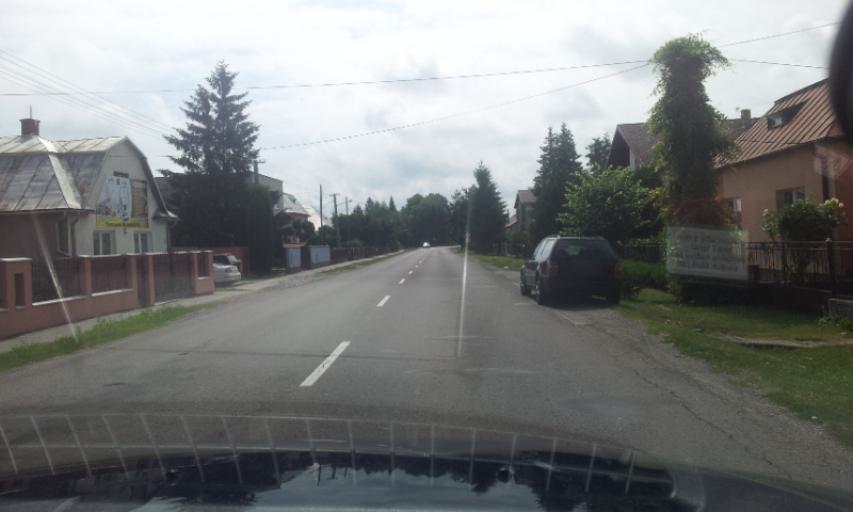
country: SK
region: Kosicky
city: Michalovce
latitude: 48.7371
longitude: 21.9495
